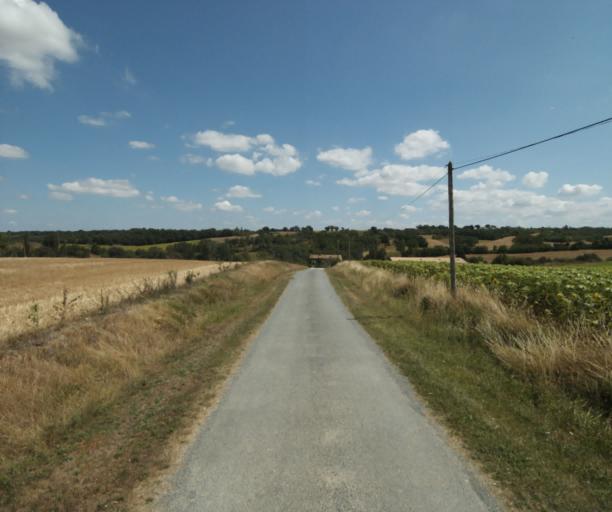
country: FR
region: Midi-Pyrenees
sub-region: Departement de la Haute-Garonne
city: Auriac-sur-Vendinelle
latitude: 43.4774
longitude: 1.8434
